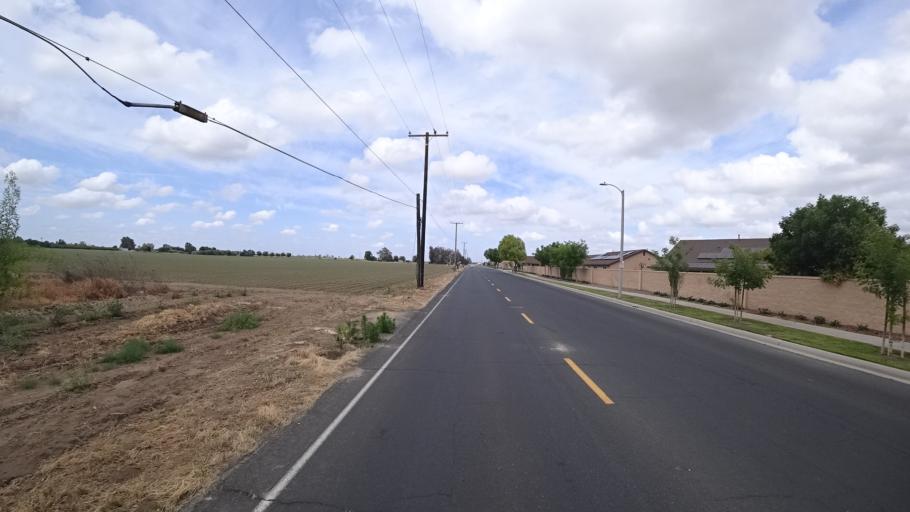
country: US
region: California
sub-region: Kings County
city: Hanford
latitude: 36.3056
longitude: -119.6664
